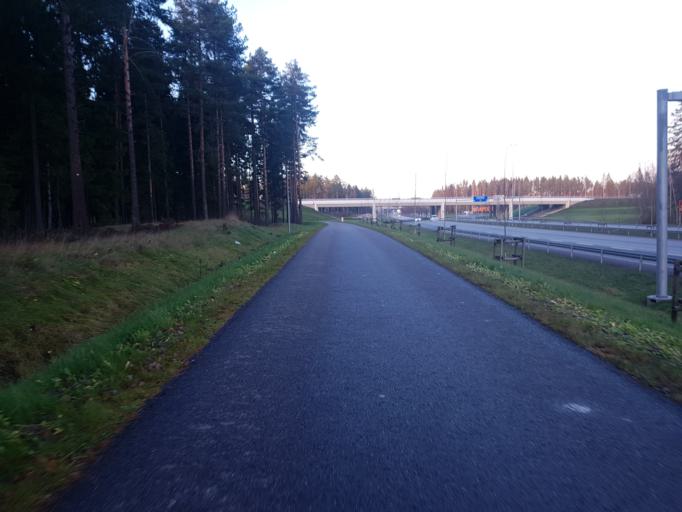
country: FI
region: Uusimaa
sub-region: Helsinki
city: Vantaa
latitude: 60.3000
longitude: 24.9591
